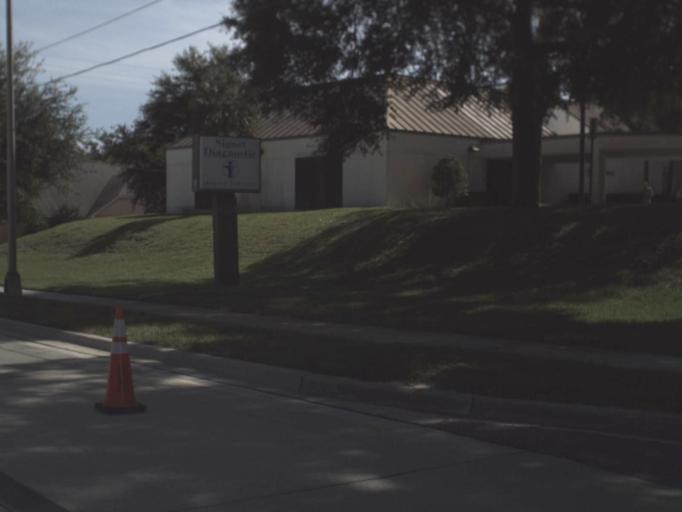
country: US
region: Florida
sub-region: Duval County
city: Jacksonville
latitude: 30.2902
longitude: -81.7202
